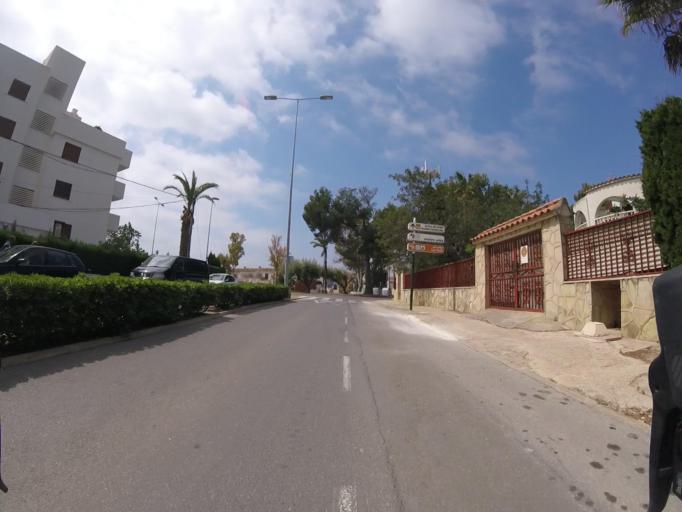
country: ES
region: Valencia
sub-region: Provincia de Castello
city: Alcoceber
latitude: 40.2516
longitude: 0.2815
